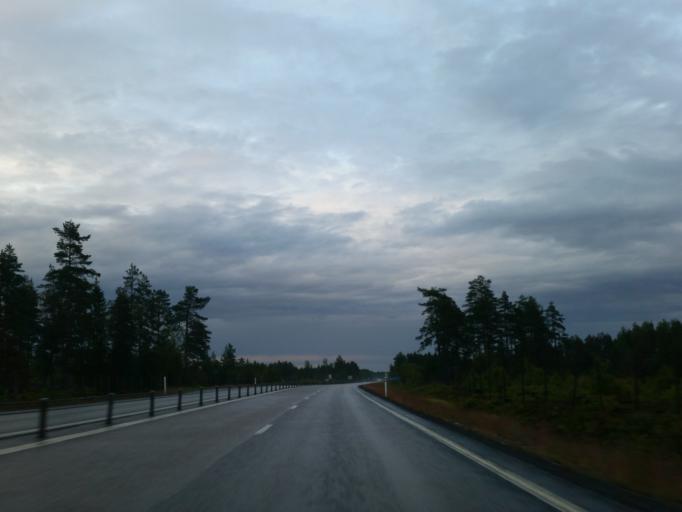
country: SE
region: Vaesterbotten
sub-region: Umea Kommun
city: Saevar
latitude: 63.9568
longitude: 20.6755
